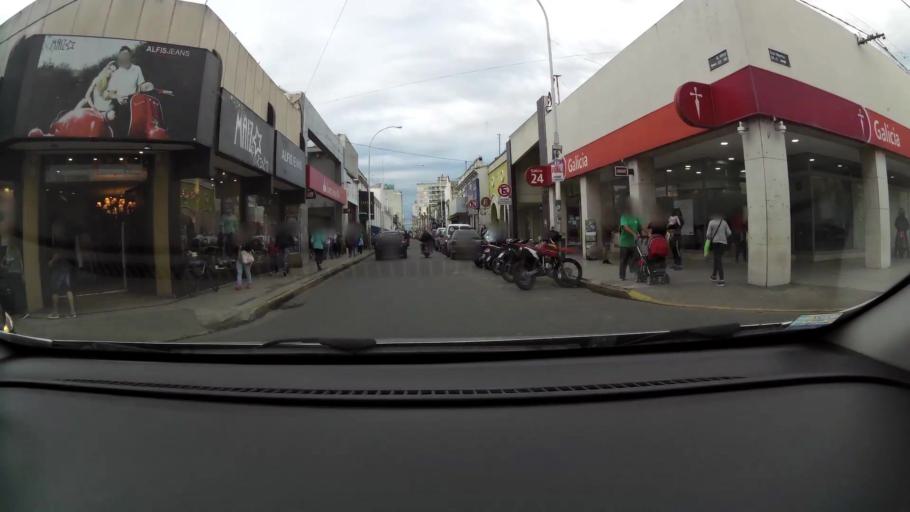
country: AR
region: Buenos Aires
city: San Nicolas de los Arroyos
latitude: -33.3324
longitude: -60.2207
